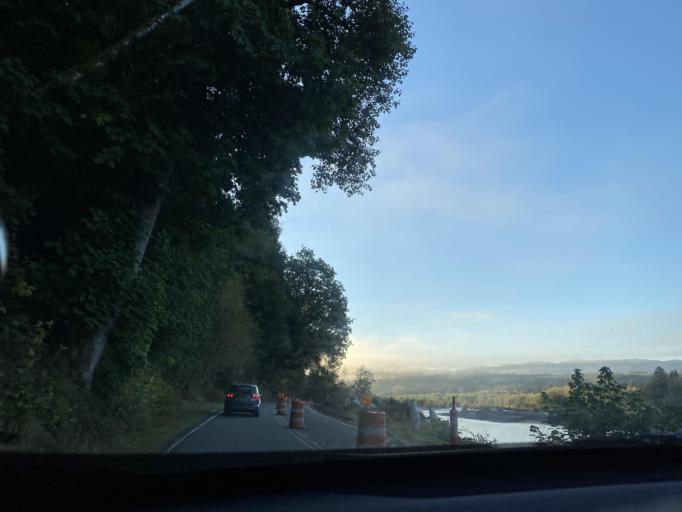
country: US
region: Washington
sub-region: Clallam County
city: Forks
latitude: 47.8222
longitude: -124.1828
